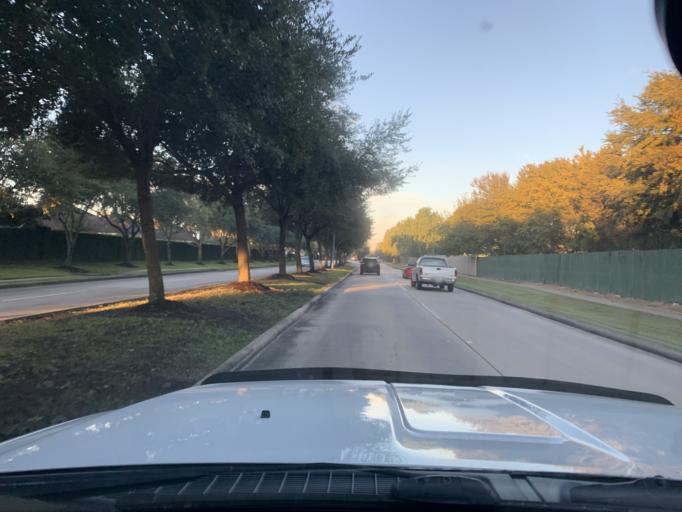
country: US
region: Texas
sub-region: Fort Bend County
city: Sugar Land
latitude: 29.6512
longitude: -95.6264
